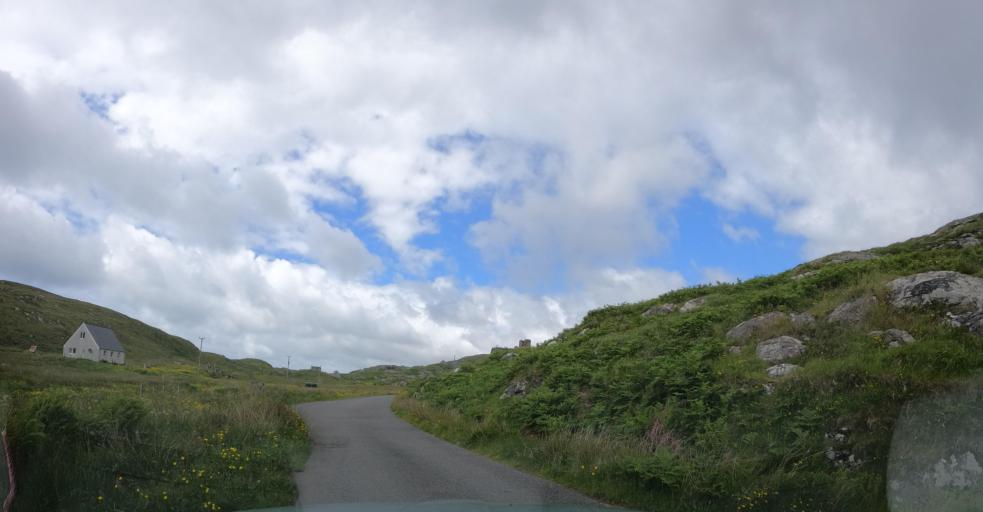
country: GB
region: Scotland
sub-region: Eilean Siar
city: Isle of South Uist
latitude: 57.0702
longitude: -7.2955
